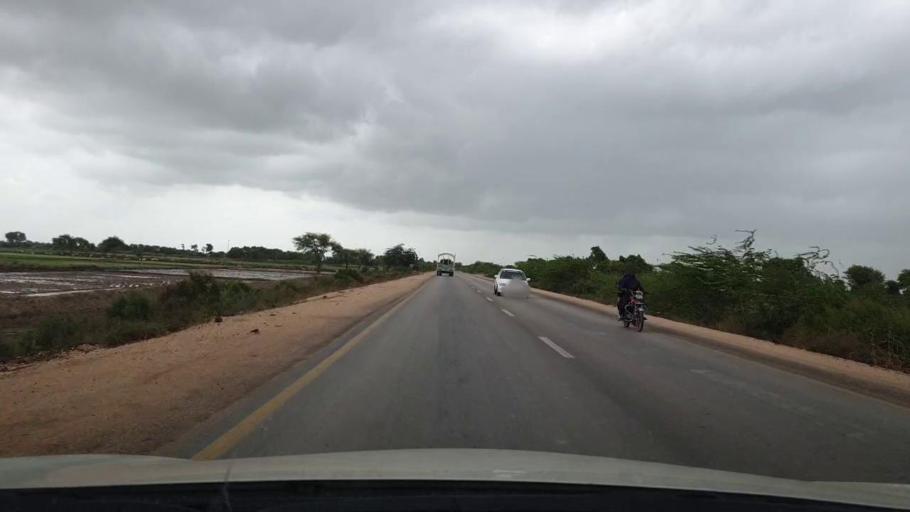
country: PK
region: Sindh
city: Mirpur Batoro
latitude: 24.6427
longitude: 68.4603
